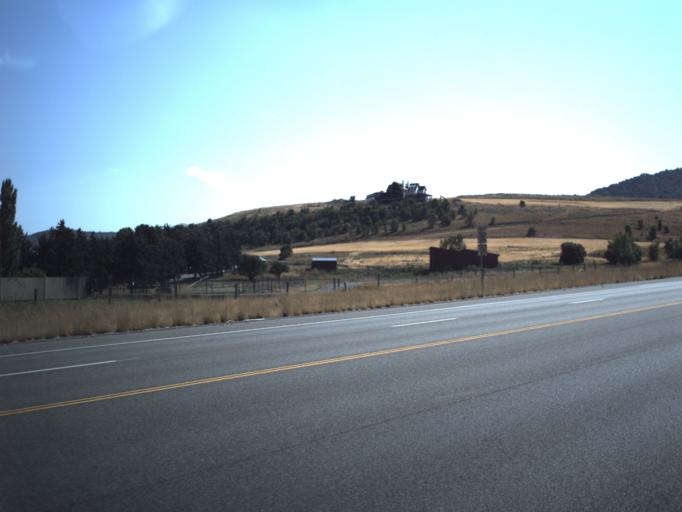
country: US
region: Utah
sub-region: Cache County
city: Wellsville
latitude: 41.6089
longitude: -111.9397
